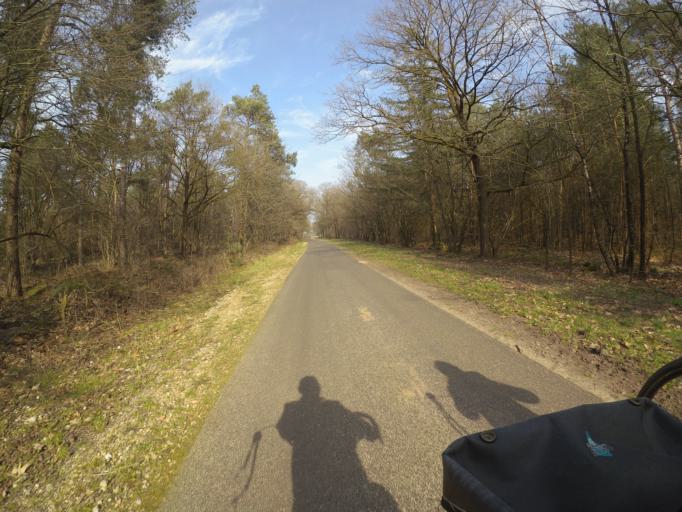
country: NL
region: North Brabant
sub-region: Gemeente Breda
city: Breda
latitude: 51.5432
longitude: 4.8530
